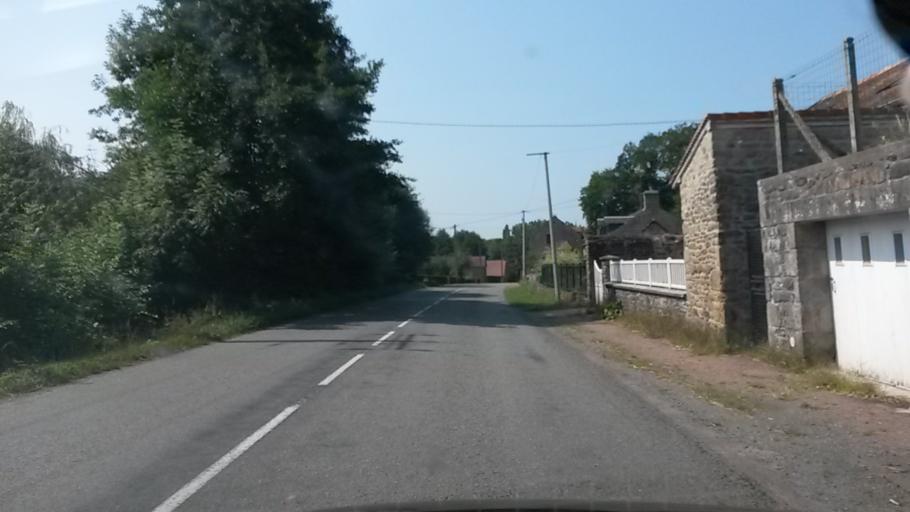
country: FR
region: Pays de la Loire
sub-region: Departement de la Mayenne
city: Saint-Pierre-des-Nids
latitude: 48.4038
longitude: -0.0857
